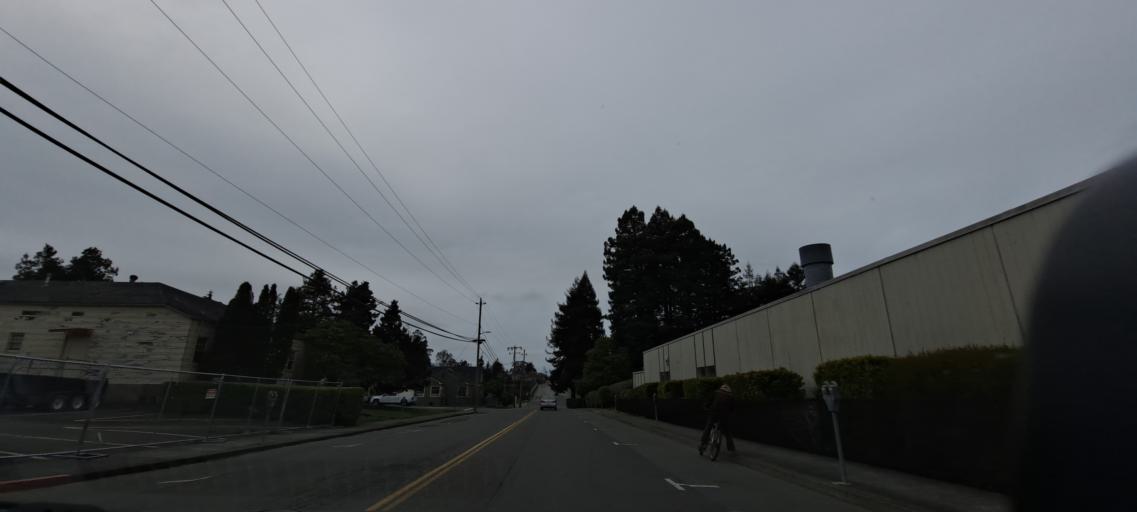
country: US
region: California
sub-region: Humboldt County
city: Arcata
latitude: 40.8718
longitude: -124.0795
